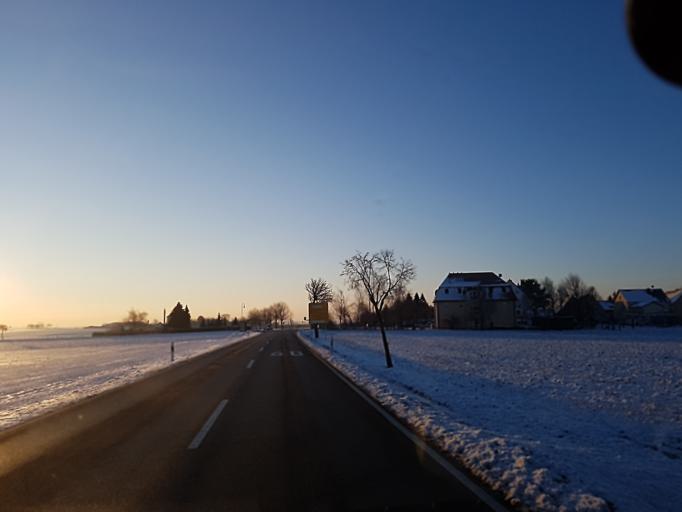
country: DE
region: Saxony
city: Grossweitzschen
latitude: 51.1610
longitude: 13.0513
